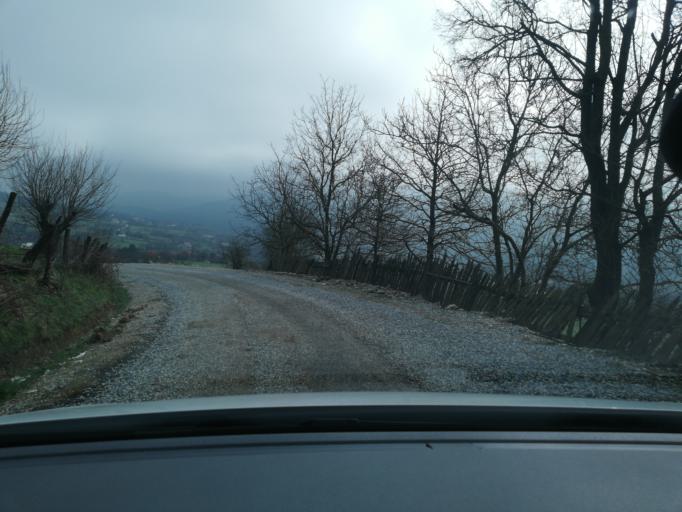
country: TR
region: Bolu
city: Bolu
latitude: 40.6674
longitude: 31.4612
